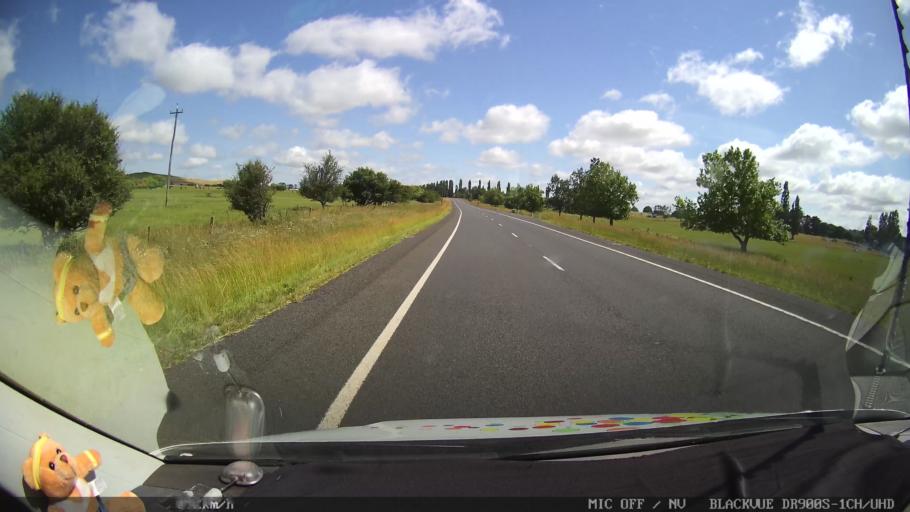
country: AU
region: New South Wales
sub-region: Glen Innes Severn
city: Glen Innes
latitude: -29.8481
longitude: 151.7380
